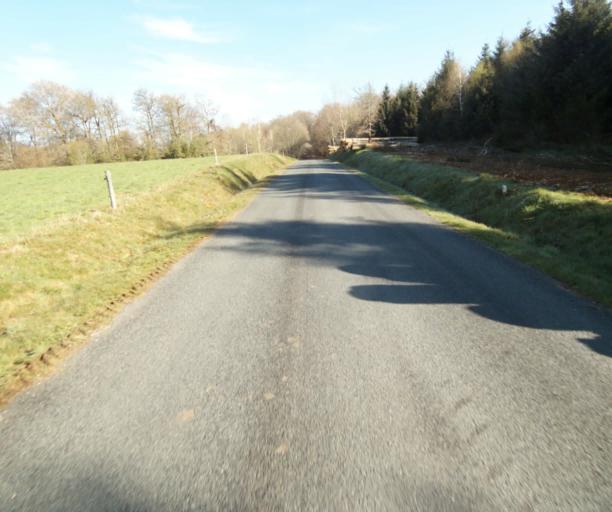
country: FR
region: Limousin
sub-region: Departement de la Correze
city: Correze
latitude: 45.2952
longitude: 1.8709
